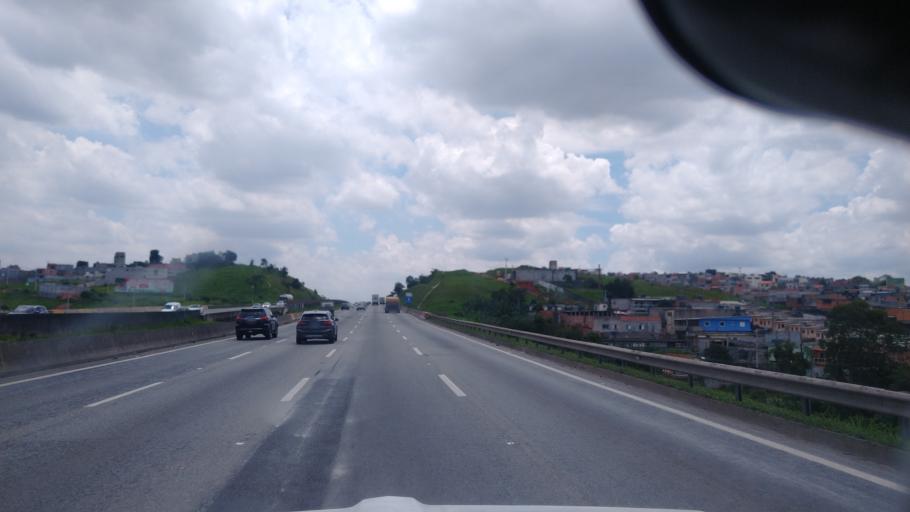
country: BR
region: Sao Paulo
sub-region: Itaquaquecetuba
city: Itaquaquecetuba
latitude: -23.4666
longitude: -46.3889
